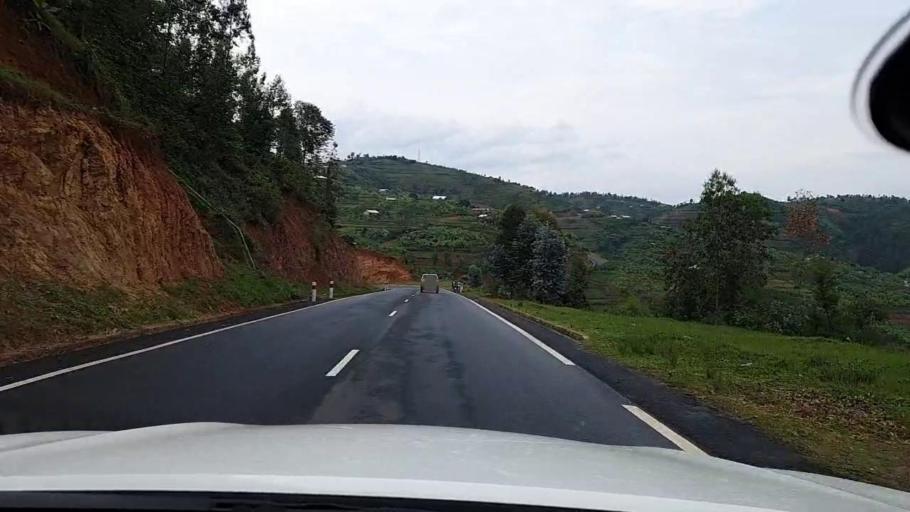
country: RW
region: Western Province
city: Kibuye
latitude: -2.1621
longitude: 29.2959
